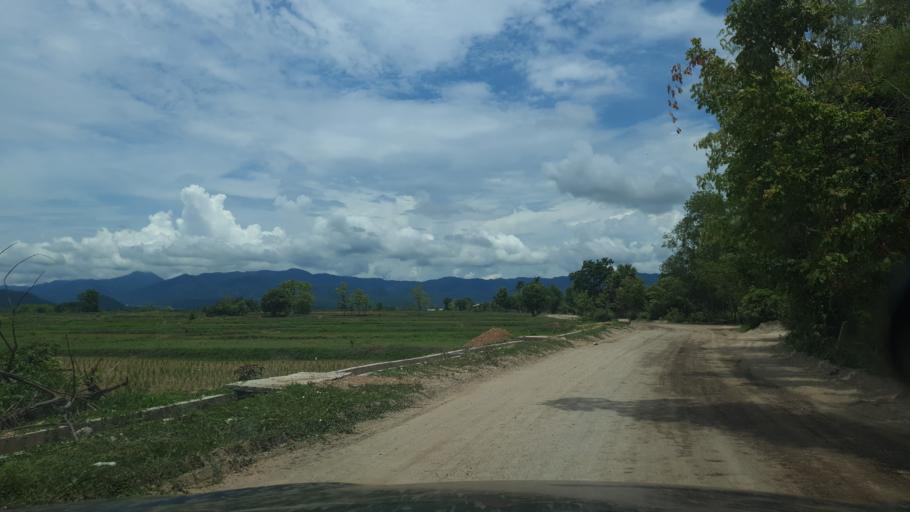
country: TH
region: Lampang
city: Sop Prap
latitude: 17.9396
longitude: 99.3569
